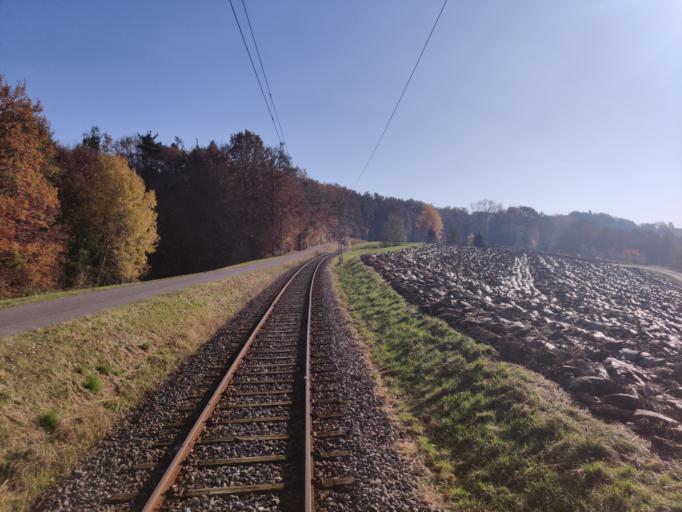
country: AT
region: Styria
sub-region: Politischer Bezirk Suedoststeiermark
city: Maierdorf
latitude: 46.8958
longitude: 15.8338
